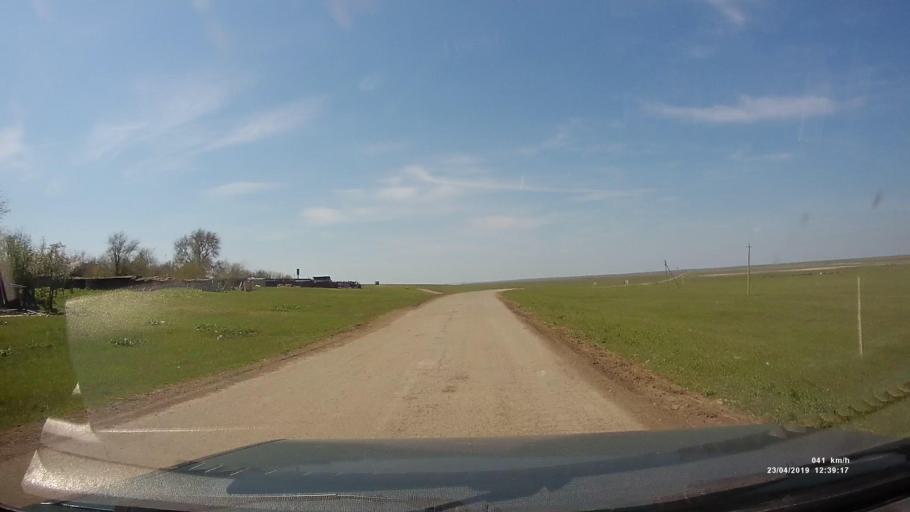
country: RU
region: Kalmykiya
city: Yashalta
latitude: 46.4341
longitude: 42.7100
